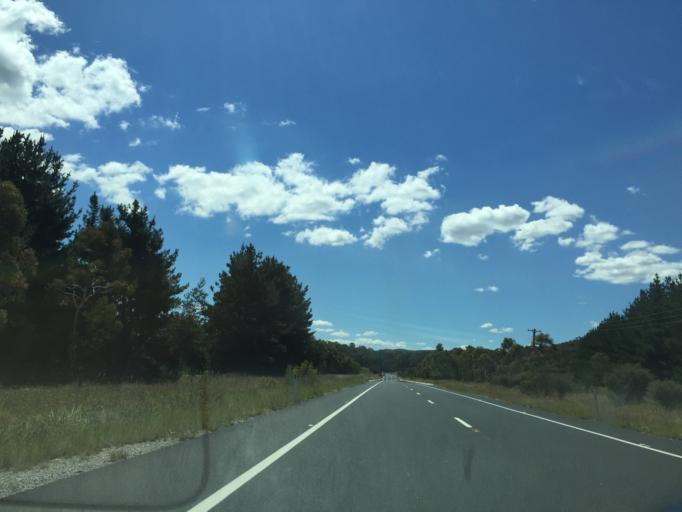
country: AU
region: New South Wales
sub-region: Lithgow
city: Lithgow
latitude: -33.4063
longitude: 150.0964
